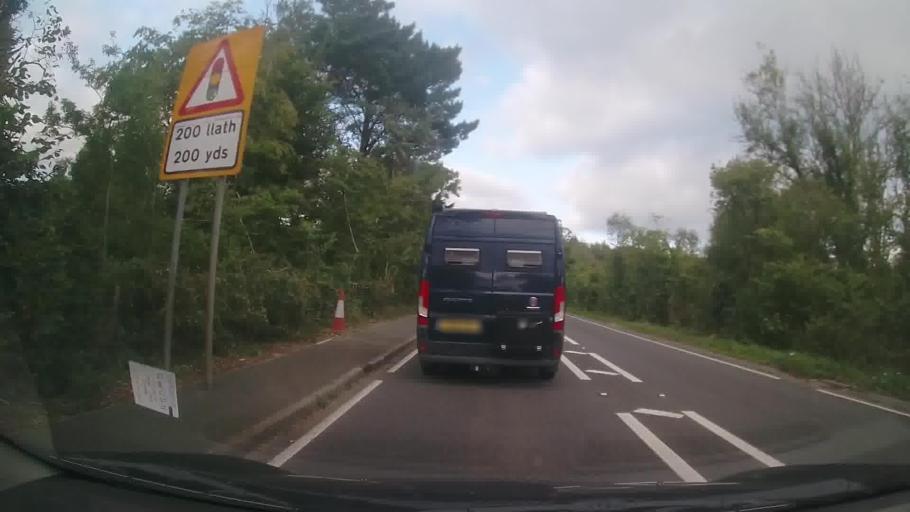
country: GB
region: Wales
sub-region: Pembrokeshire
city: Jeffreyston
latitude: 51.7184
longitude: -4.7543
